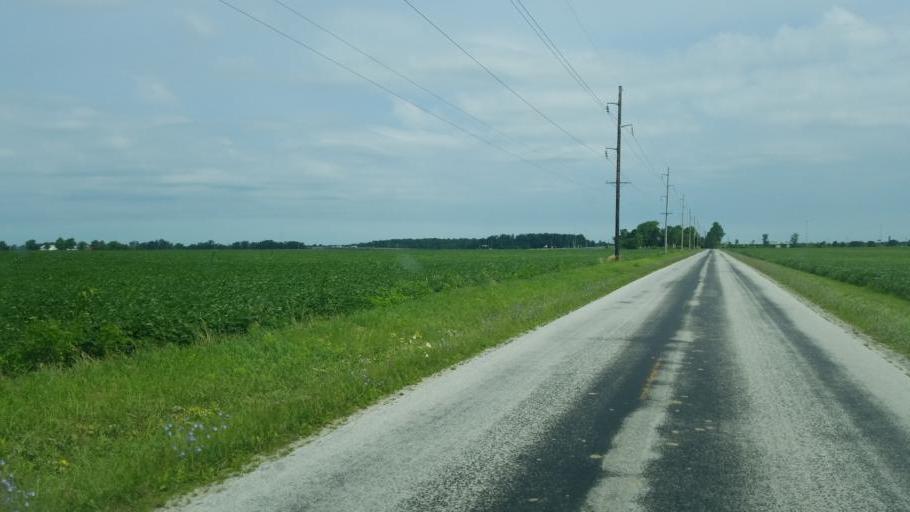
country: US
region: Ohio
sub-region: Wyandot County
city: Carey
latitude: 40.9321
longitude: -83.4009
